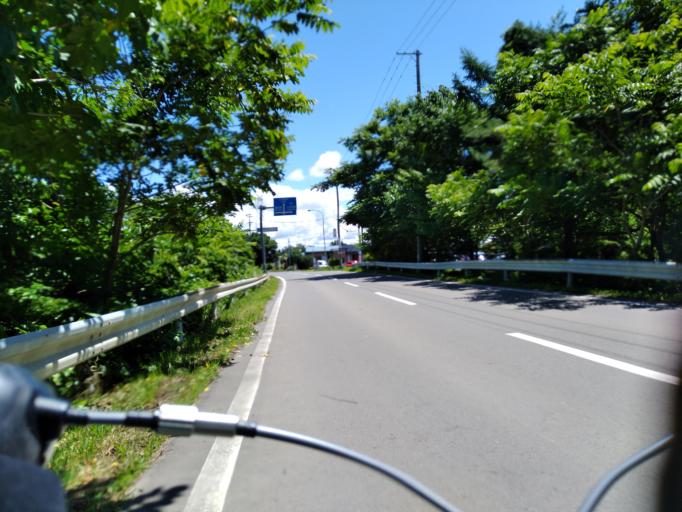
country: JP
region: Iwate
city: Shizukuishi
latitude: 39.7580
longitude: 140.9838
